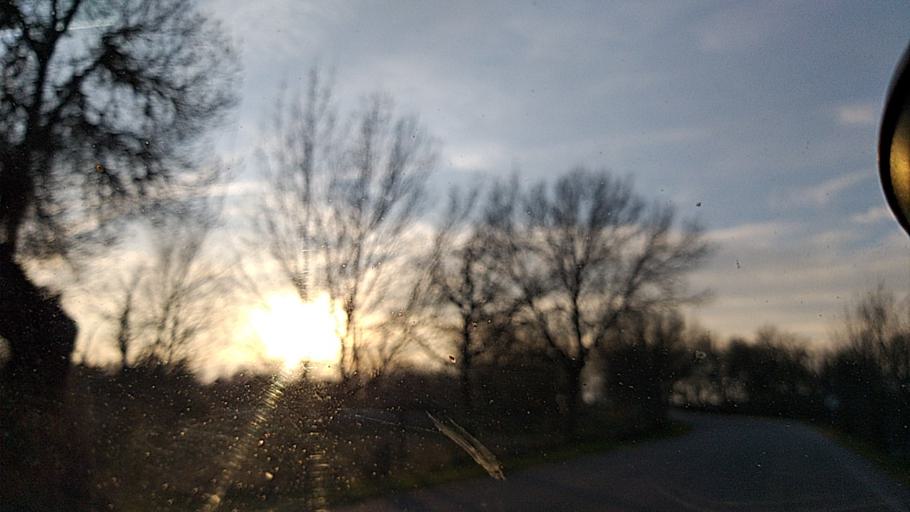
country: PT
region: Guarda
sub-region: Guarda
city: Sequeira
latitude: 40.6000
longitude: -7.0910
